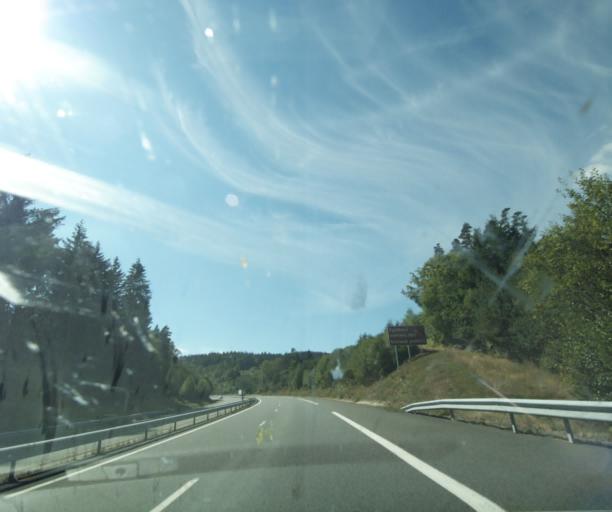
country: FR
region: Limousin
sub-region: Departement de la Correze
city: Egletons
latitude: 45.4385
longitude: 2.0510
